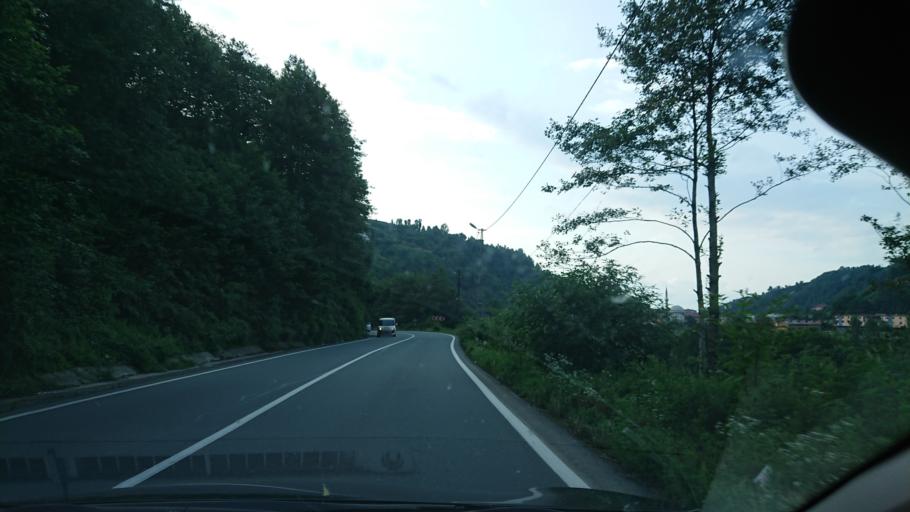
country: TR
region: Rize
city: Cayeli
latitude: 41.0682
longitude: 40.7134
